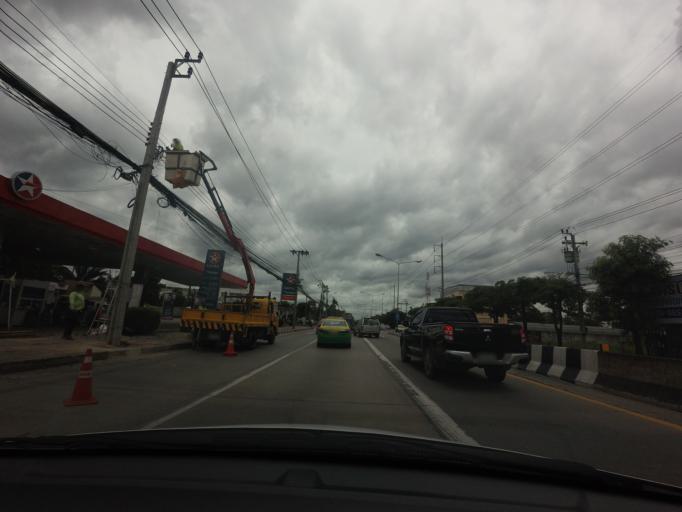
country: TH
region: Bangkok
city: Min Buri
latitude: 13.7871
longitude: 100.7460
